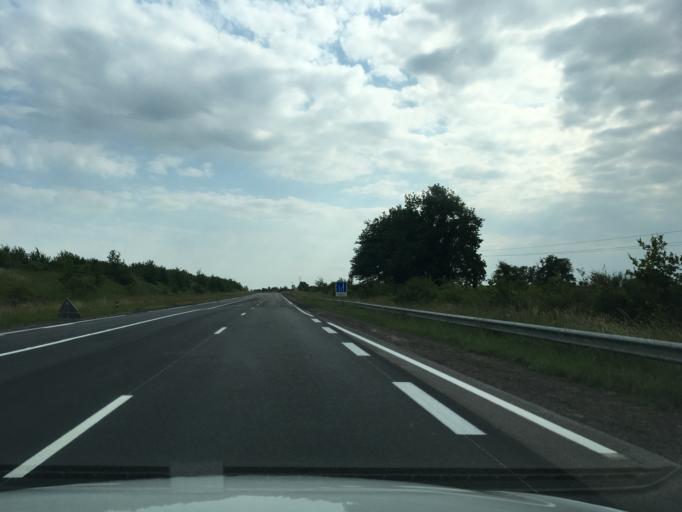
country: FR
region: Poitou-Charentes
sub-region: Departement des Deux-Sevres
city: Parthenay
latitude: 46.6489
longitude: -0.2720
